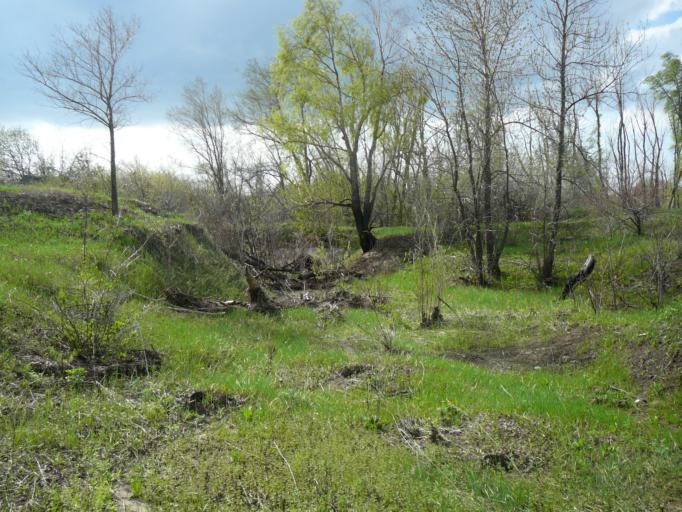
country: RU
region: Saratov
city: Engel's
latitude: 51.4578
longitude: 46.1732
